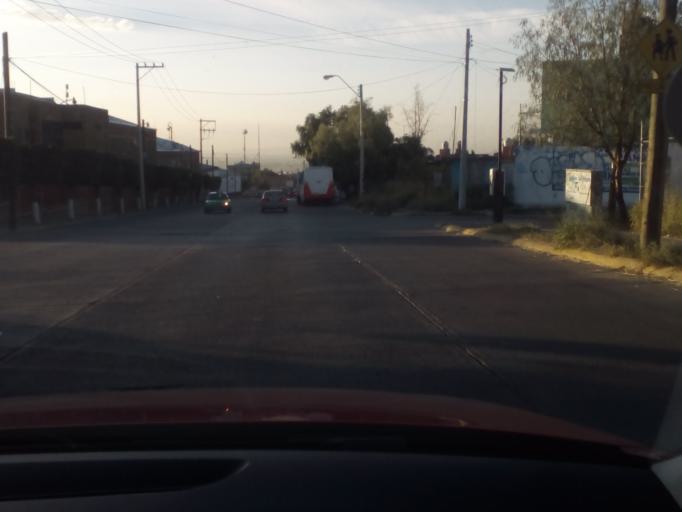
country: MX
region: Guanajuato
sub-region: Leon
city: Ejido la Joya
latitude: 21.1306
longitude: -101.7151
